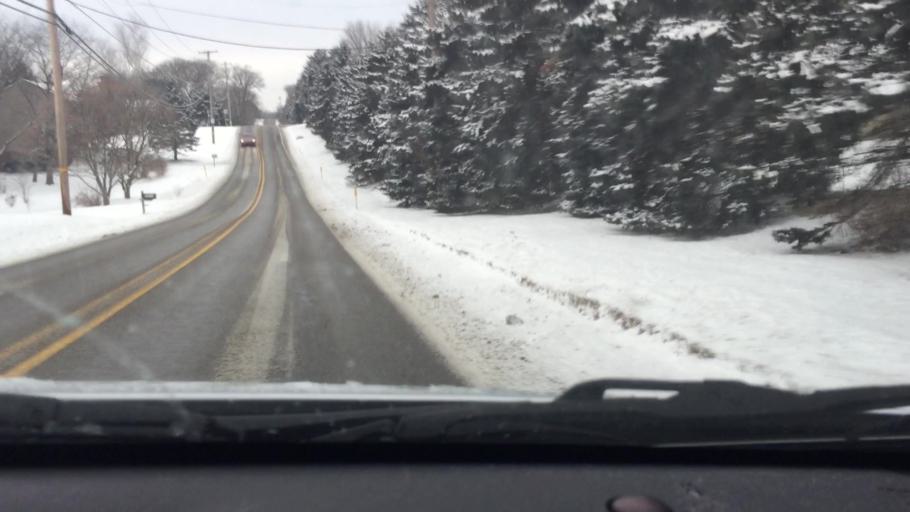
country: US
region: Pennsylvania
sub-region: Butler County
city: Fernway
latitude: 40.7246
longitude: -80.1187
